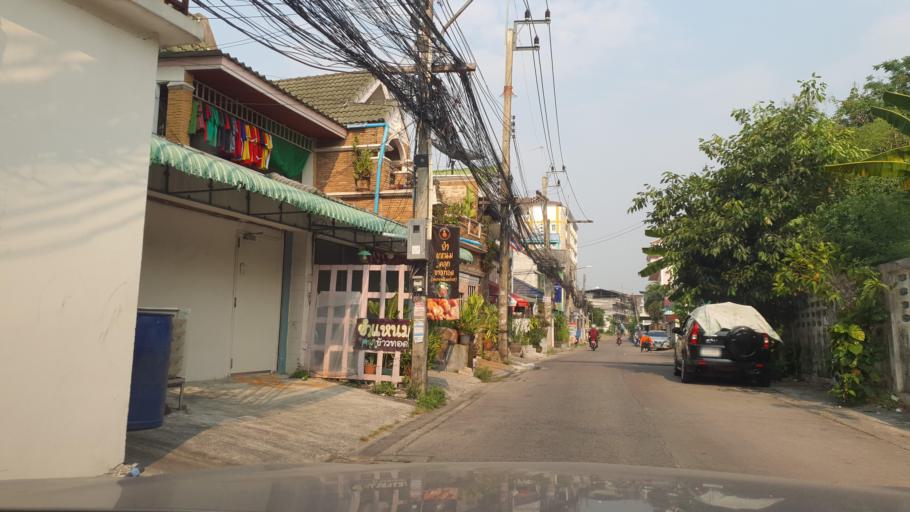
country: TH
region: Chon Buri
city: Phatthaya
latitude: 12.9391
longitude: 100.8999
